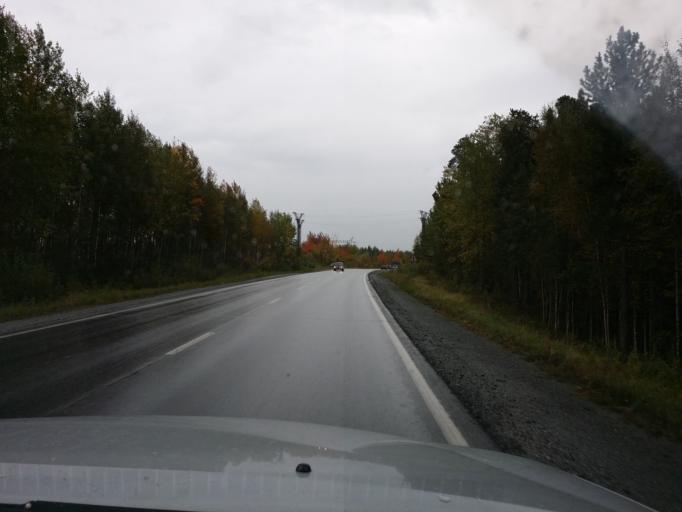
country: RU
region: Khanty-Mansiyskiy Avtonomnyy Okrug
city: Langepas
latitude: 61.1734
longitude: 75.5612
